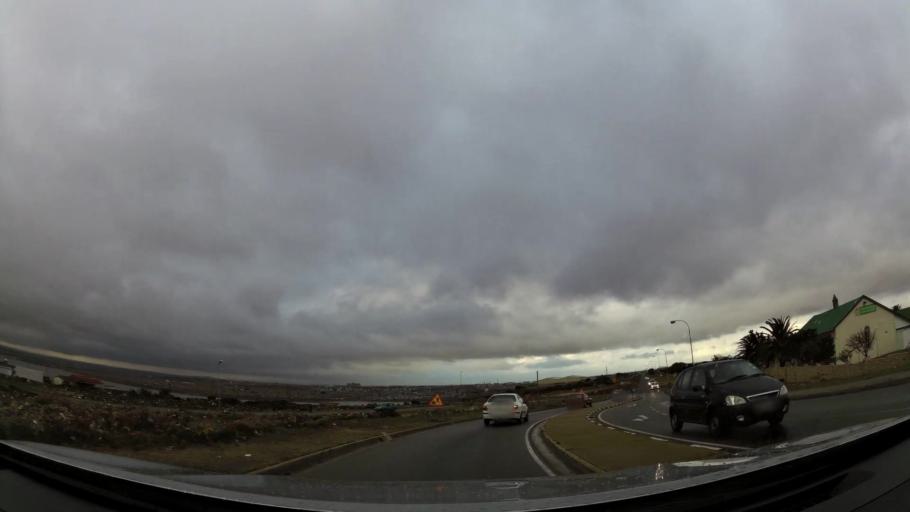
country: ZA
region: Eastern Cape
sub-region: Nelson Mandela Bay Metropolitan Municipality
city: Port Elizabeth
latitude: -33.8957
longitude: 25.5399
